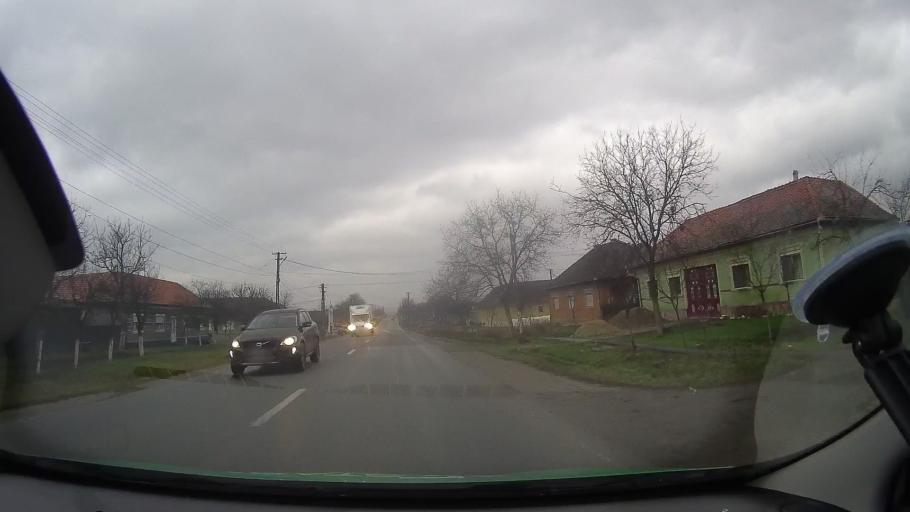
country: RO
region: Arad
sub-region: Comuna Almas
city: Almas
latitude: 46.2886
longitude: 22.2269
